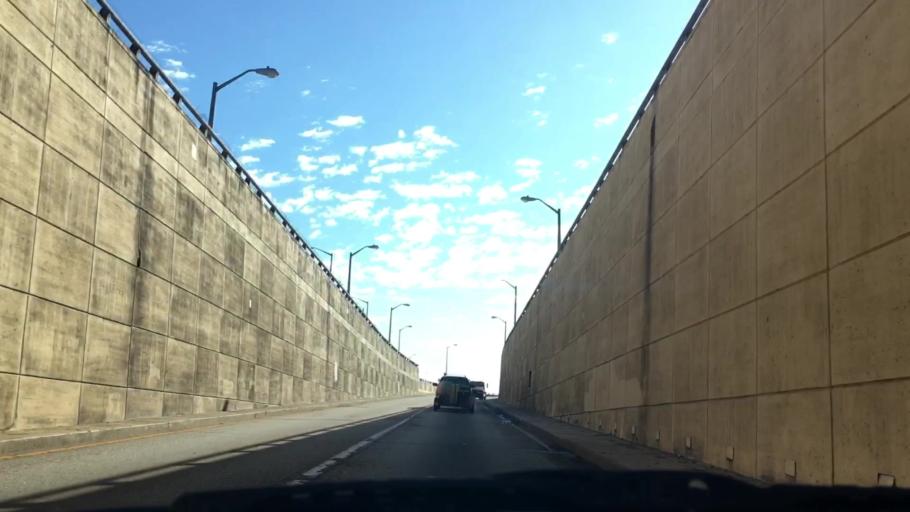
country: US
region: Virginia
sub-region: City of Hampton
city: East Hampton
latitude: 36.9913
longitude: -76.3082
